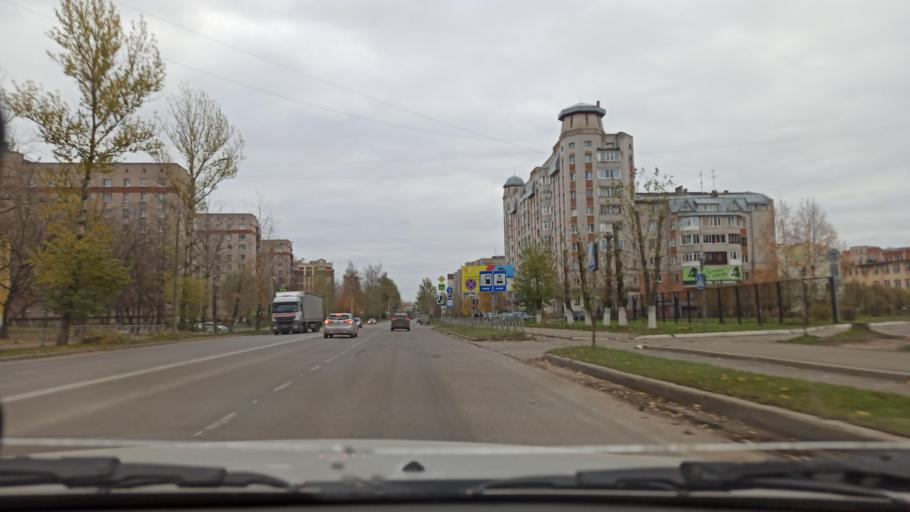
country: RU
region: Vologda
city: Vologda
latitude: 59.2159
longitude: 39.8729
